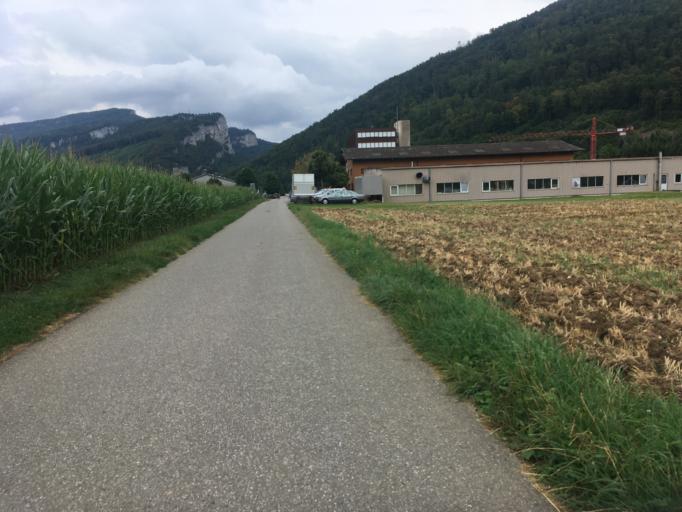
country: CH
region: Solothurn
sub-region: Bezirk Thal
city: Balsthal
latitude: 47.3088
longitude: 7.6752
